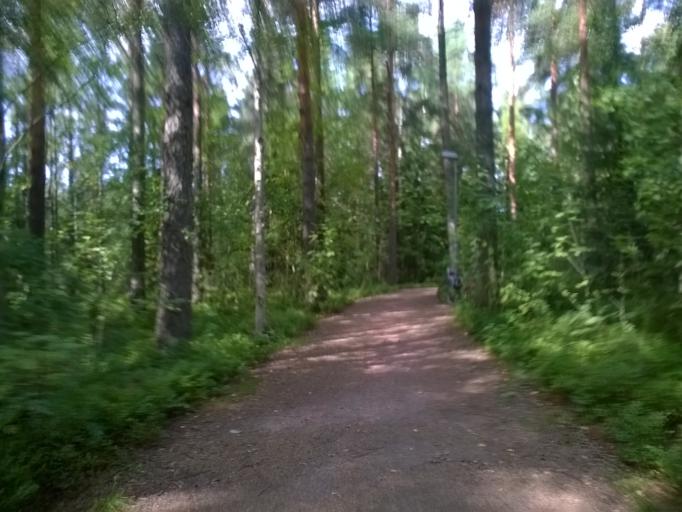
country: FI
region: Uusimaa
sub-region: Helsinki
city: Teekkarikylae
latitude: 60.2597
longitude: 24.8795
